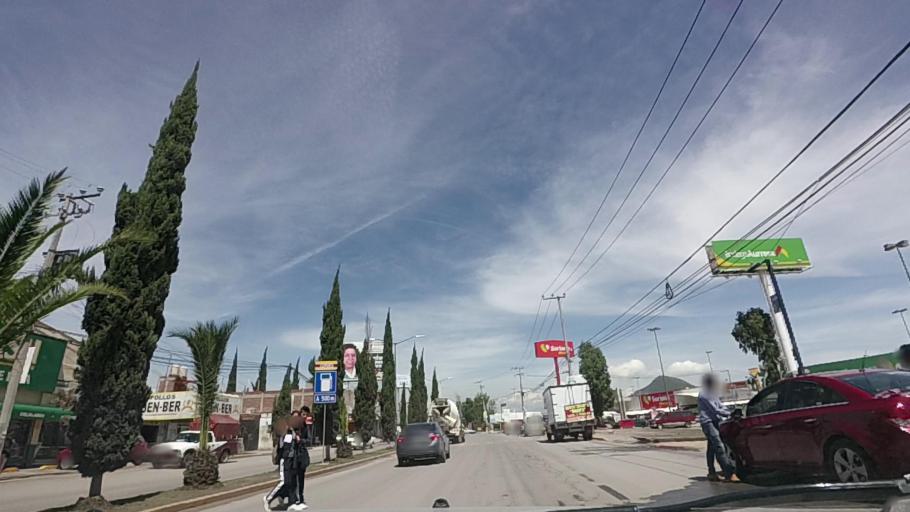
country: MX
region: Mexico
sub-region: Huehuetoca
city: Casa Nueva
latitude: 19.8318
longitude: -99.2090
